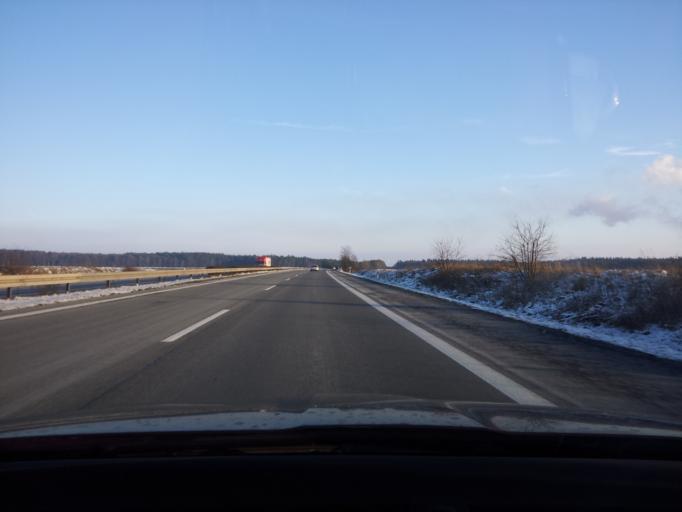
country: DE
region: Brandenburg
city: Heiligengrabe
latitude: 53.1678
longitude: 12.3669
